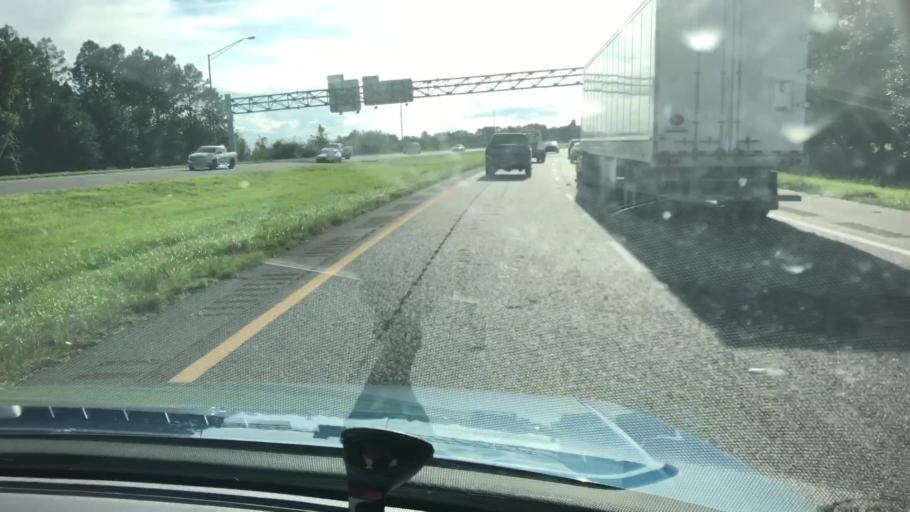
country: US
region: Florida
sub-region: Orange County
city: Lake Butler
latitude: 28.5310
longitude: -81.5609
